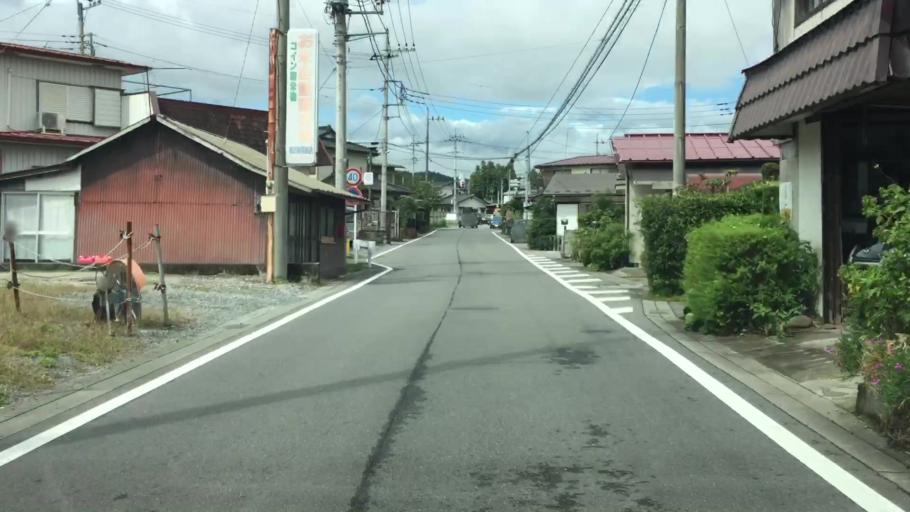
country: JP
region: Tochigi
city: Imaichi
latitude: 36.7356
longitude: 139.6864
